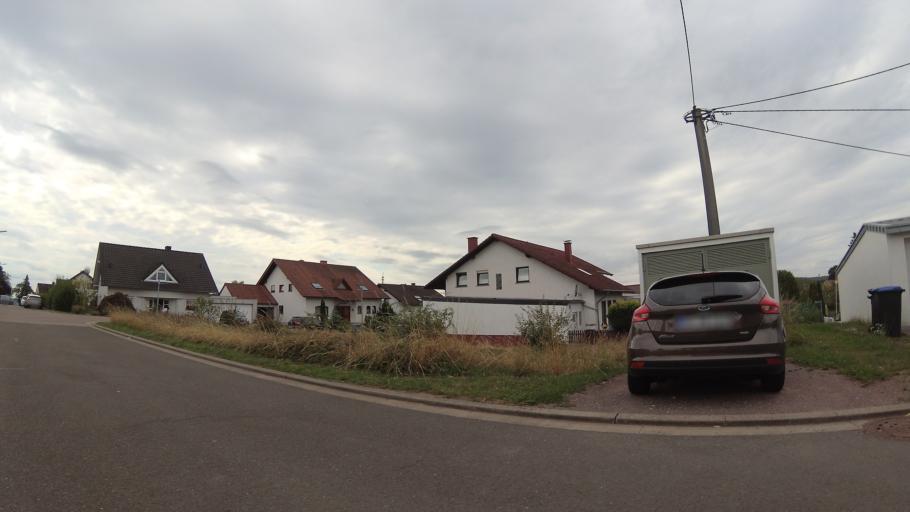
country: DE
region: Saarland
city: Kleinblittersdorf
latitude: 49.1403
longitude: 7.0605
